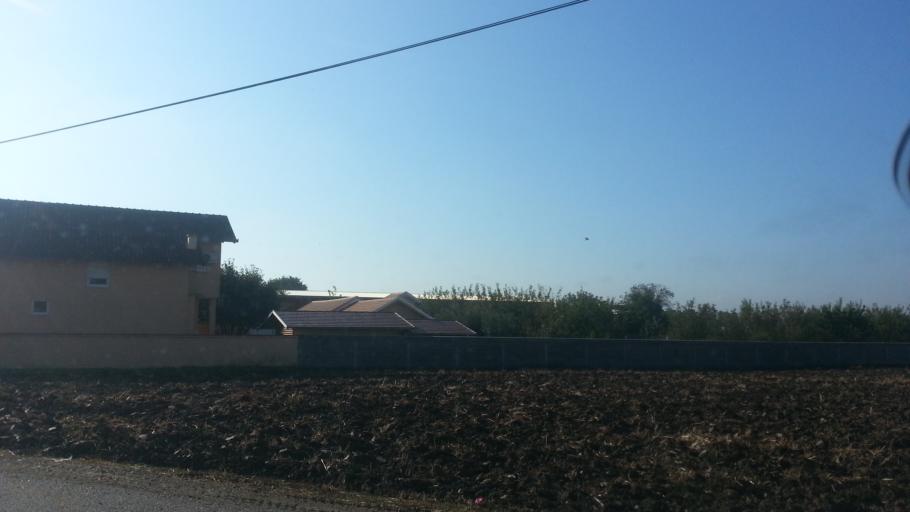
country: RS
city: Stari Banovci
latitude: 44.9830
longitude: 20.2680
